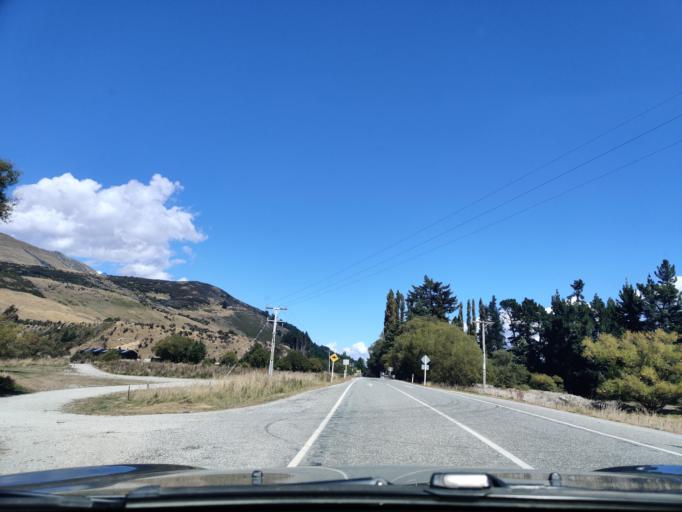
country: NZ
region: Otago
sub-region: Queenstown-Lakes District
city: Queenstown
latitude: -44.7995
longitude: 168.3986
